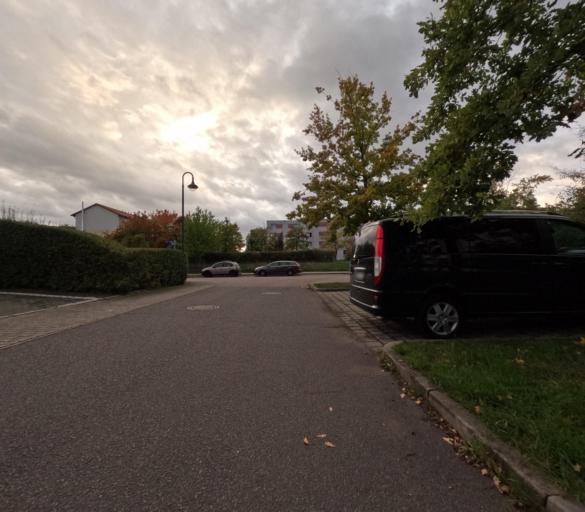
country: DE
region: Saxony
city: Markranstadt
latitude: 51.3075
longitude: 12.2322
